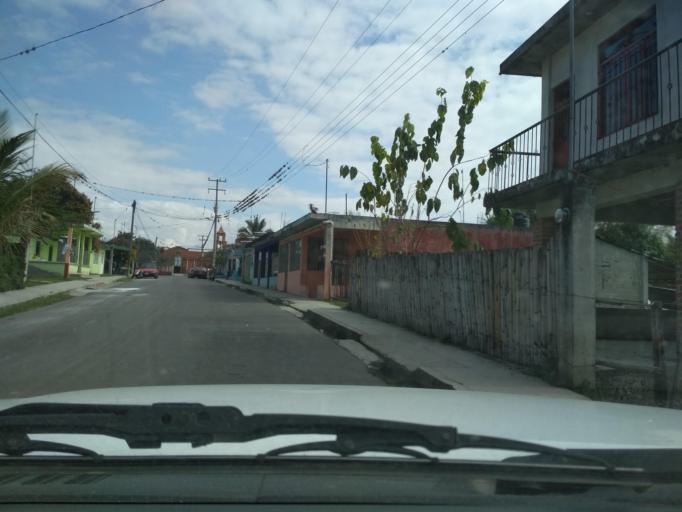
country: MX
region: Veracruz
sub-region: Coatepec
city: Tuzamapan
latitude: 19.3701
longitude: -96.8820
